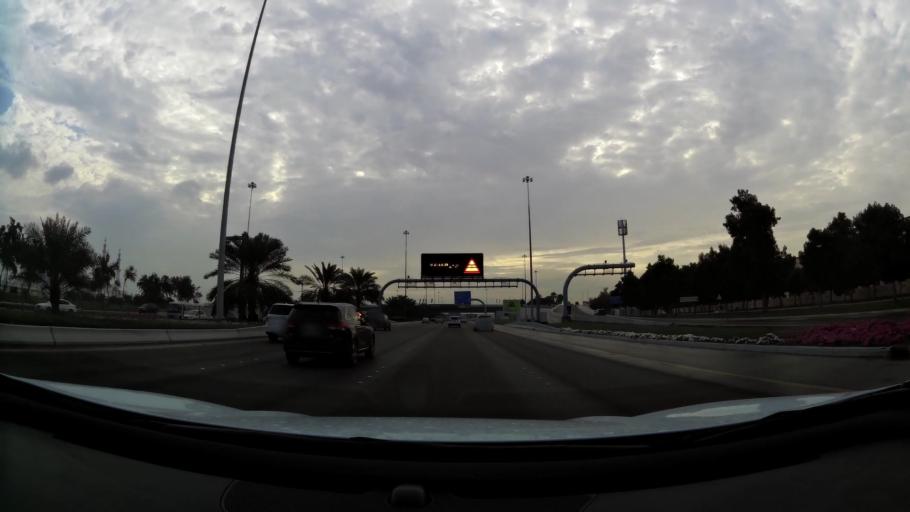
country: AE
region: Abu Dhabi
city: Abu Dhabi
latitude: 24.4082
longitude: 54.4684
